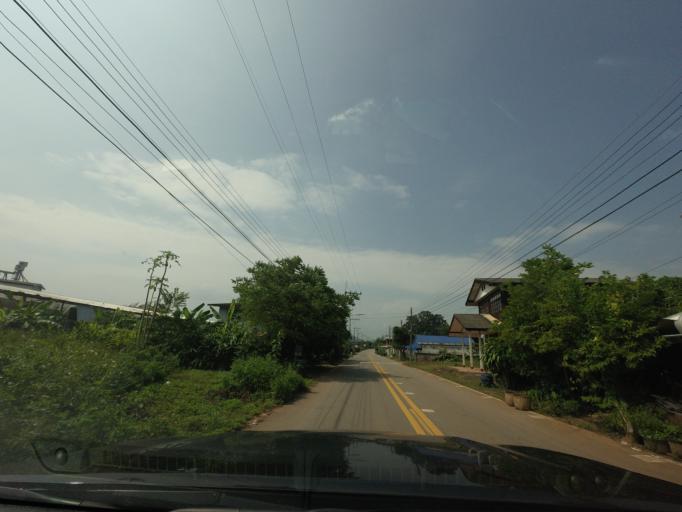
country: LA
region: Xiagnabouli
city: Muang Kenthao
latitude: 17.7026
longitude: 101.4117
